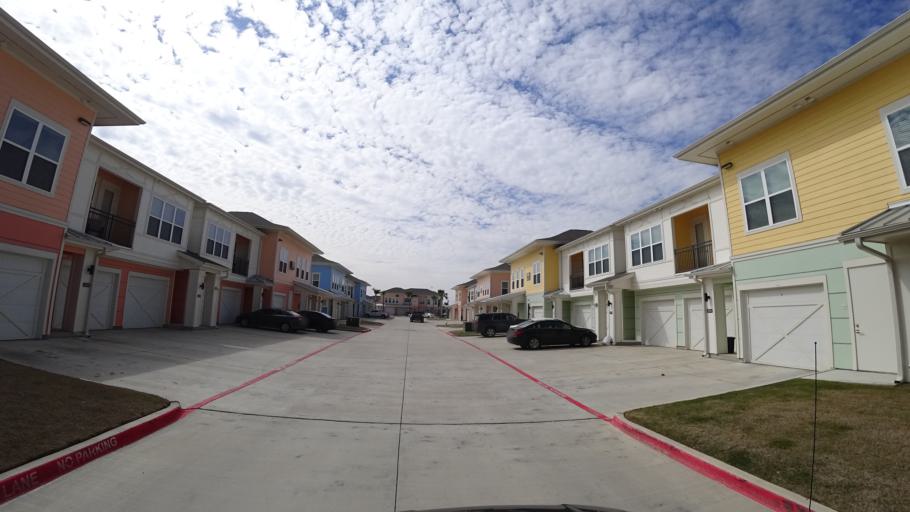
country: US
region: Texas
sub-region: Denton County
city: Lewisville
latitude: 33.0053
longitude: -96.9560
